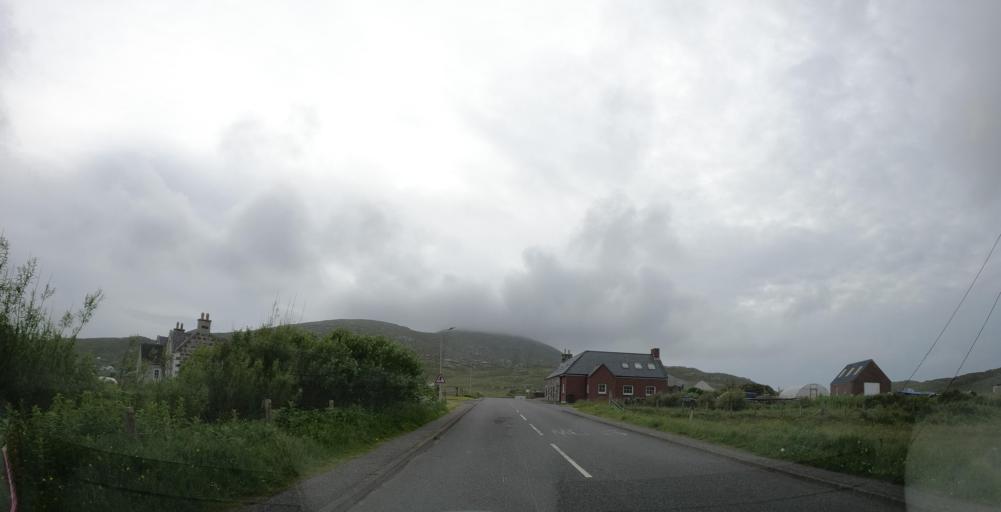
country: GB
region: Scotland
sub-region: Eilean Siar
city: Barra
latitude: 56.9562
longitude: -7.4996
